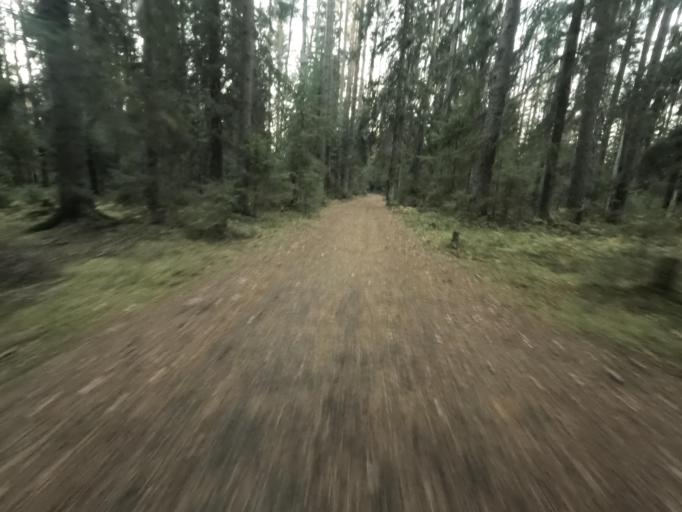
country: RU
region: St.-Petersburg
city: Komarovo
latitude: 60.1999
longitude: 29.8275
